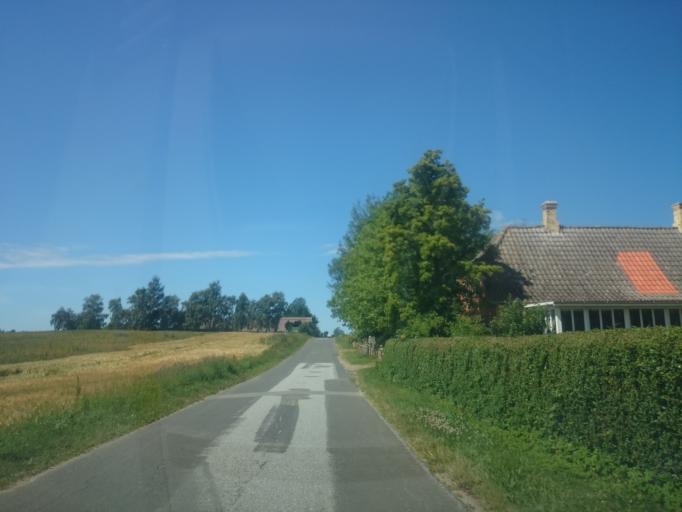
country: DK
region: South Denmark
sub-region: Langeland Kommune
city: Rudkobing
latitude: 54.9640
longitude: 10.8178
